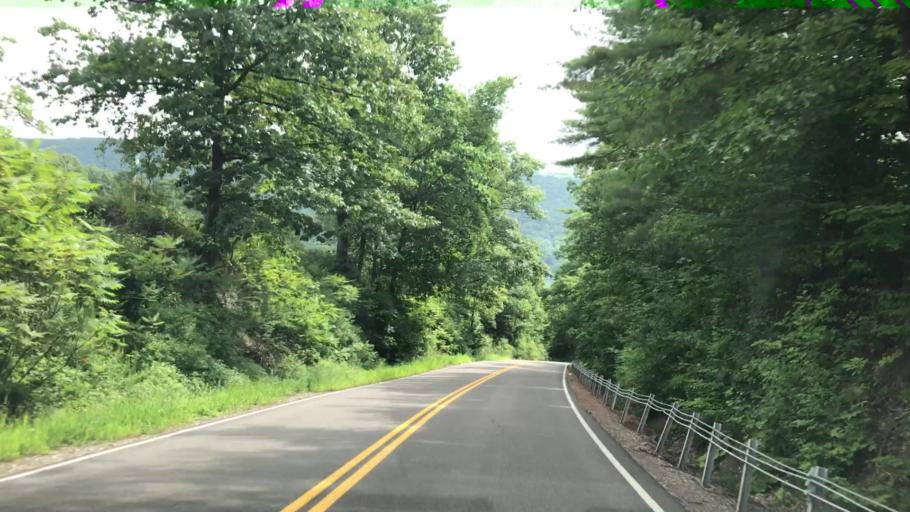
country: US
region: New York
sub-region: Steuben County
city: Sylvan Beach
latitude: 42.5287
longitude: -77.1568
